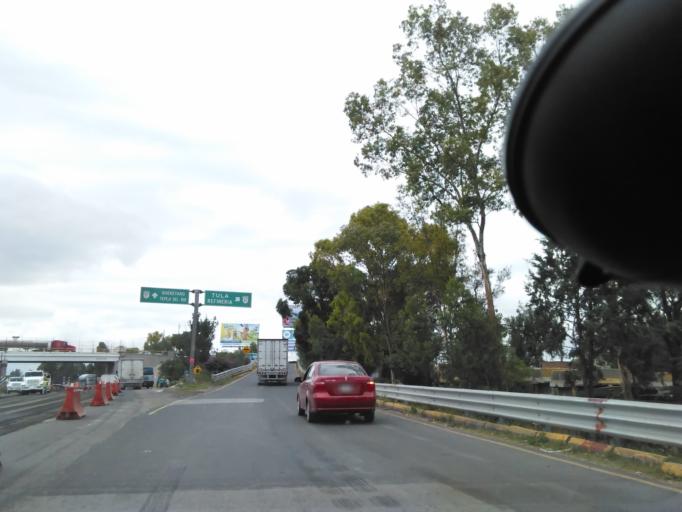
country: MX
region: Mexico
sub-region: Huehuetoca
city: Jorobas
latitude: 19.8248
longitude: -99.2476
